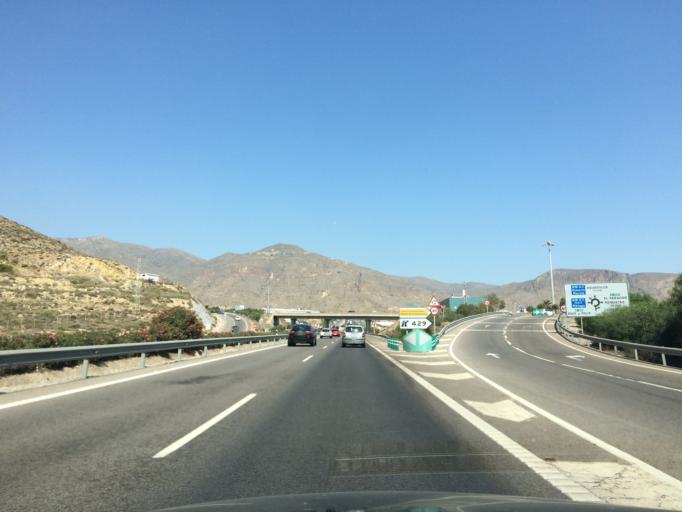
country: ES
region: Andalusia
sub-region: Provincia de Almeria
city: Aguadulce
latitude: 36.8188
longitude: -2.6001
